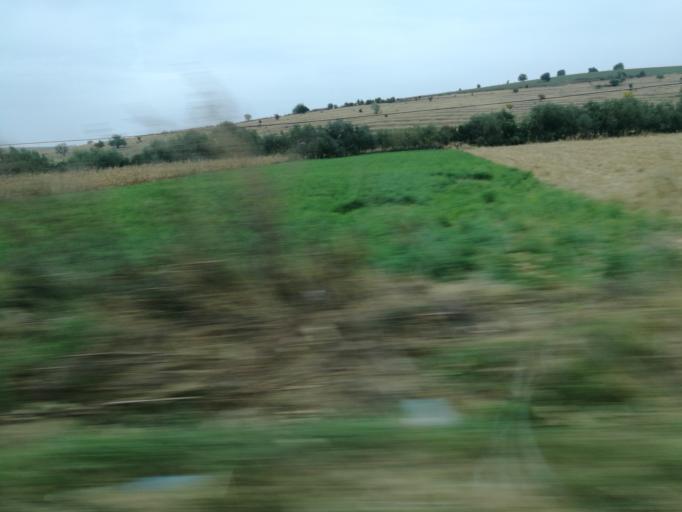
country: RO
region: Tulcea
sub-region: Comuna Ciucurova
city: Ciucurova
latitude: 44.9226
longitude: 28.4531
